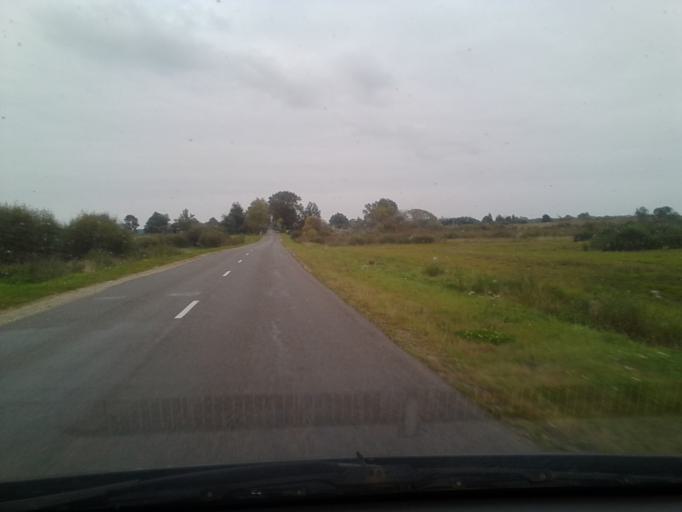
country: BY
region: Vitebsk
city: Pastavy
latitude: 55.1387
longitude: 26.9493
